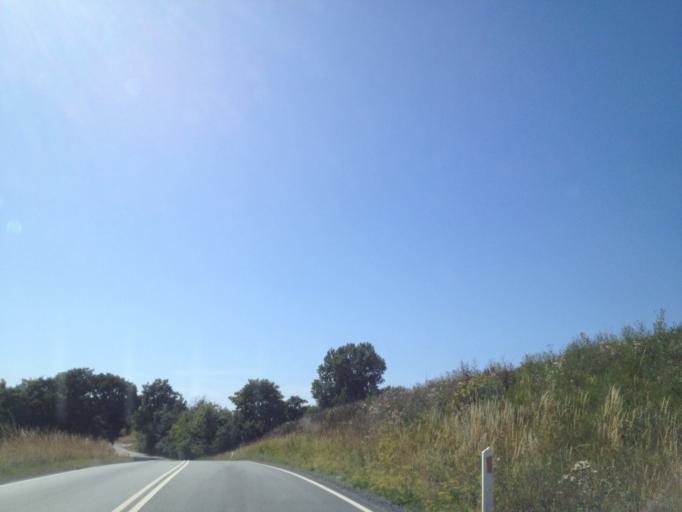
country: DK
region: Capital Region
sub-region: Helsingor Kommune
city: Hornbaek
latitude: 56.0432
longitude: 12.4301
